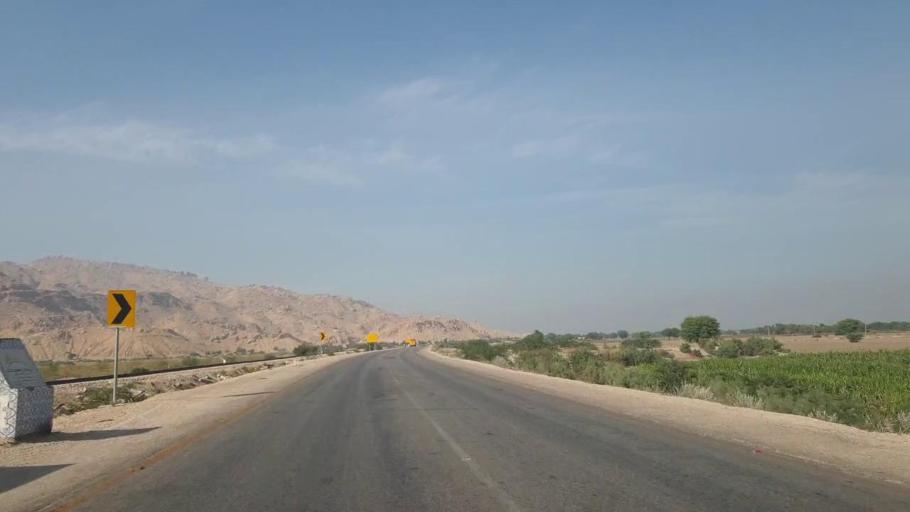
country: PK
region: Sindh
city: Sehwan
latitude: 26.2808
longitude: 67.8963
